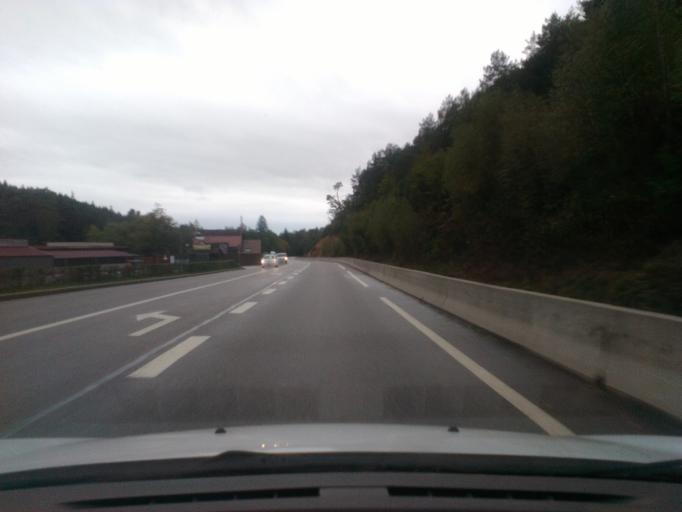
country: FR
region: Lorraine
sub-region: Departement des Vosges
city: Jeanmenil
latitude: 48.3247
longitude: 6.7300
